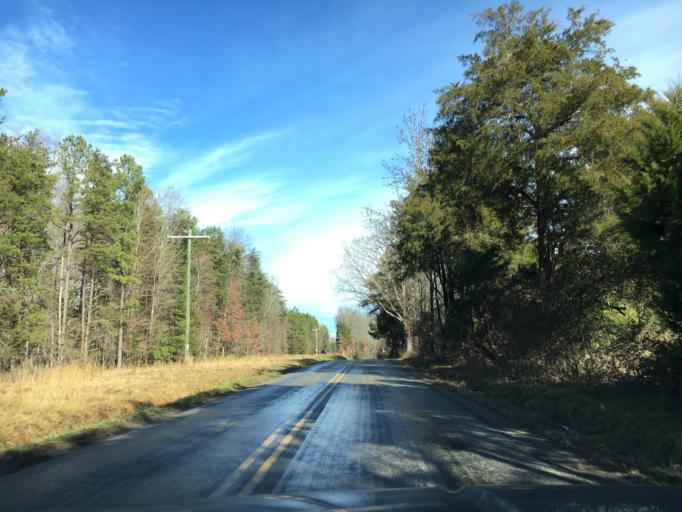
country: US
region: Virginia
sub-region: Cumberland County
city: Cumberland
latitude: 37.3448
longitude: -78.1592
